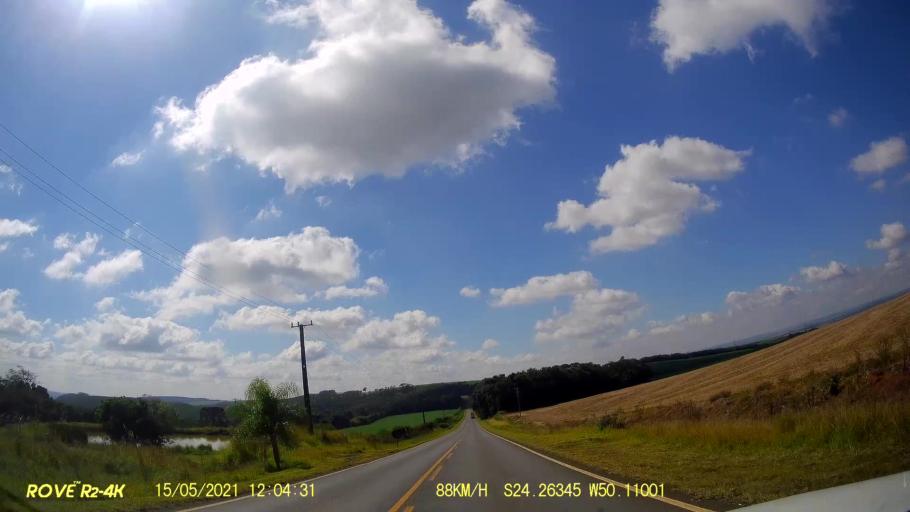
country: BR
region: Parana
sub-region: Pirai Do Sul
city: Pirai do Sul
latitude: -24.2635
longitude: -50.1099
